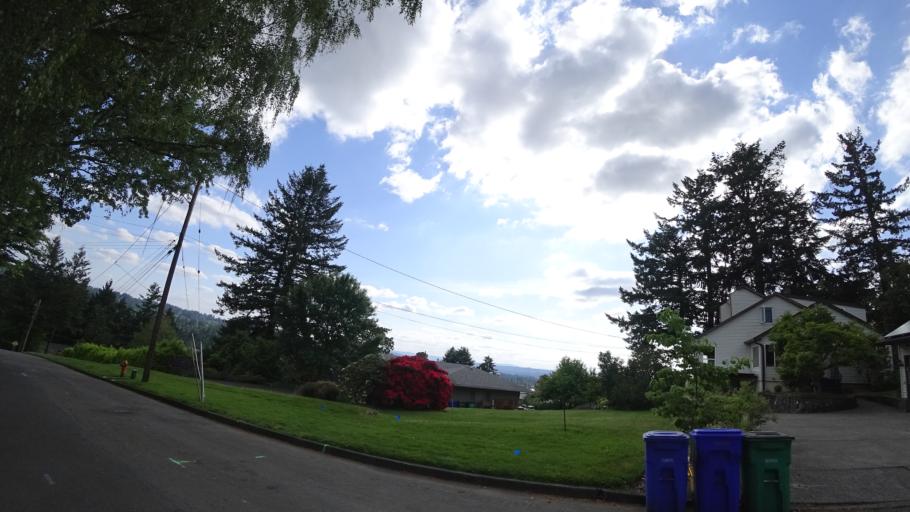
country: US
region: Oregon
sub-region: Washington County
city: Garden Home-Whitford
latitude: 45.4788
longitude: -122.7167
